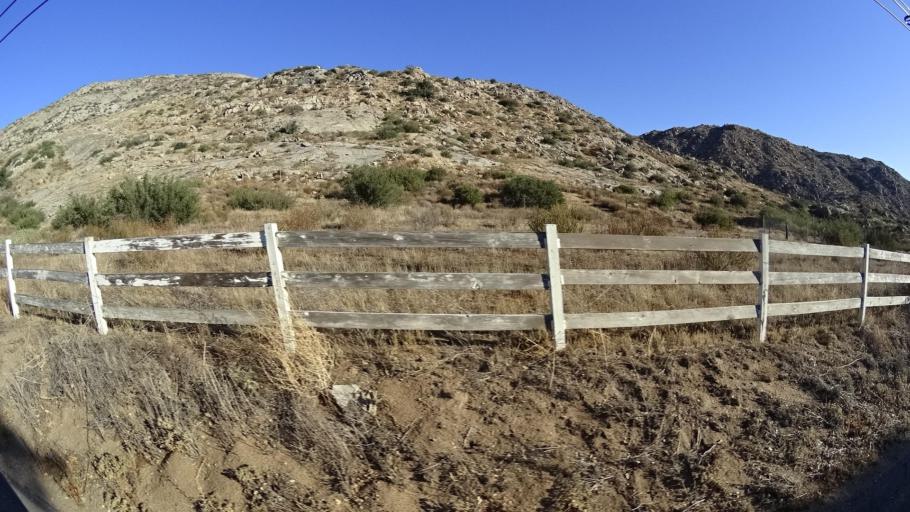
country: MX
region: Baja California
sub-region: Tecate
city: Hacienda Tecate
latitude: 32.5956
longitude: -116.5326
